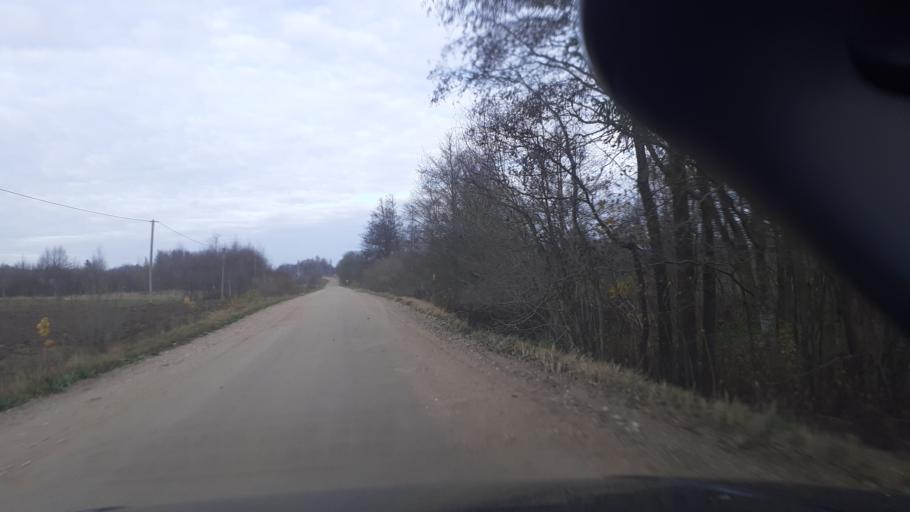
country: LV
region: Alsunga
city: Alsunga
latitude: 56.9093
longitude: 21.6560
